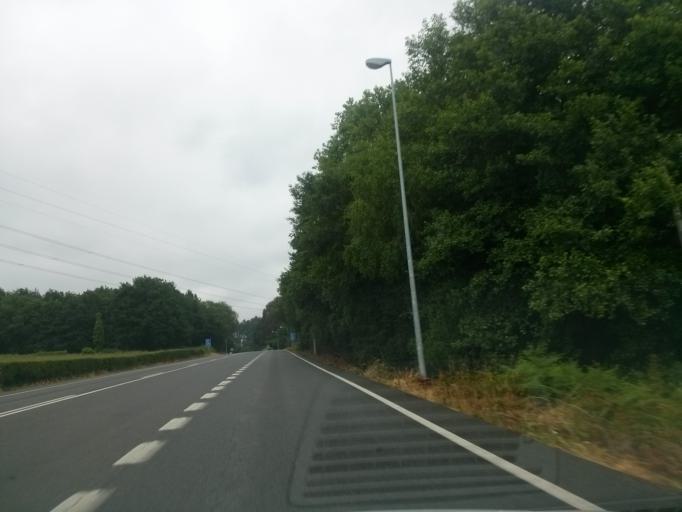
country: ES
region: Galicia
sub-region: Provincia de Lugo
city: Begonte
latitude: 43.1468
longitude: -7.6814
